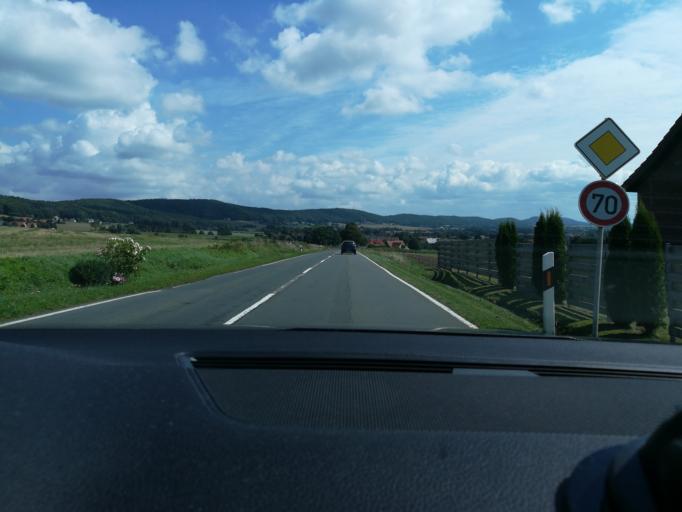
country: DE
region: North Rhine-Westphalia
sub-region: Regierungsbezirk Detmold
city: Huellhorst
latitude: 52.2870
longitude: 8.6457
